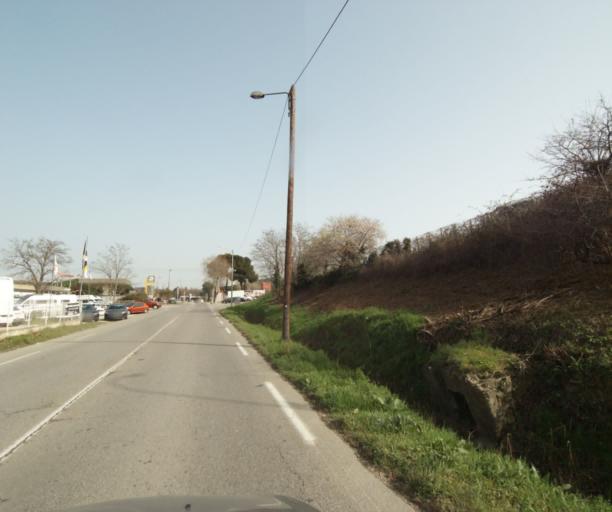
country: FR
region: Provence-Alpes-Cote d'Azur
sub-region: Departement des Bouches-du-Rhone
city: Les Pennes-Mirabeau
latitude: 43.4087
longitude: 5.3200
